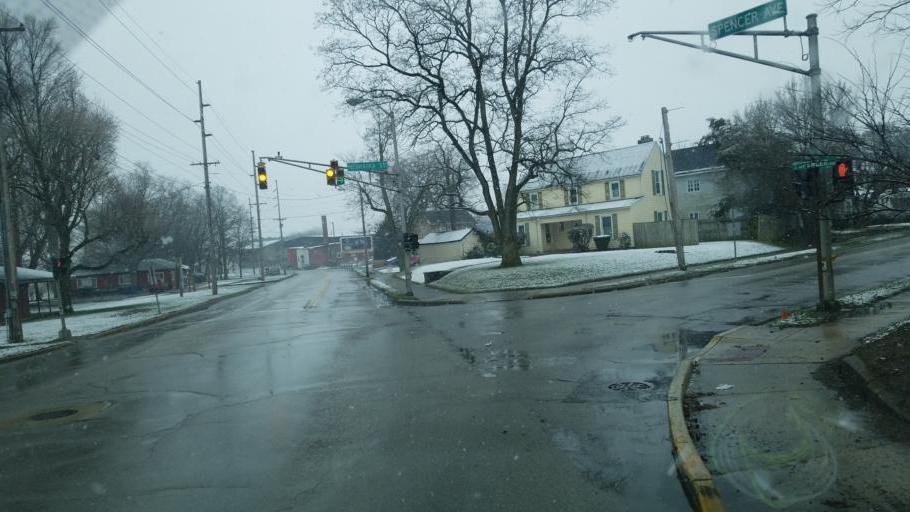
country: US
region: Indiana
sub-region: Grant County
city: Marion
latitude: 40.5622
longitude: -85.6634
